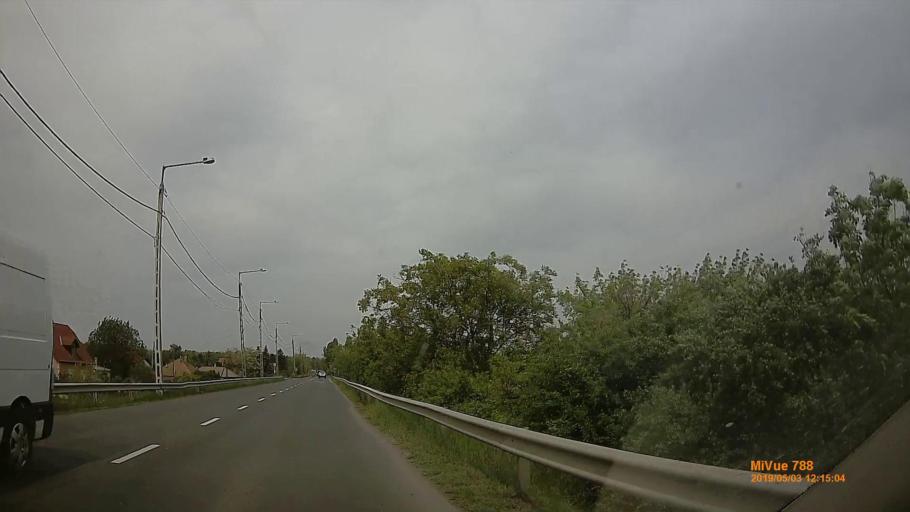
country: HU
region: Jasz-Nagykun-Szolnok
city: Szolnok
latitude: 47.1411
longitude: 20.2061
